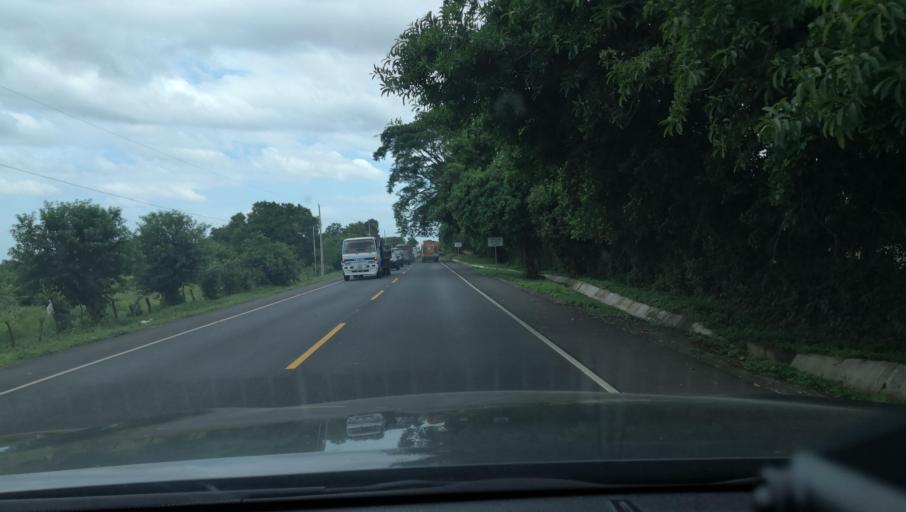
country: NI
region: Masaya
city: Nindiri
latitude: 12.0466
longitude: -86.1322
